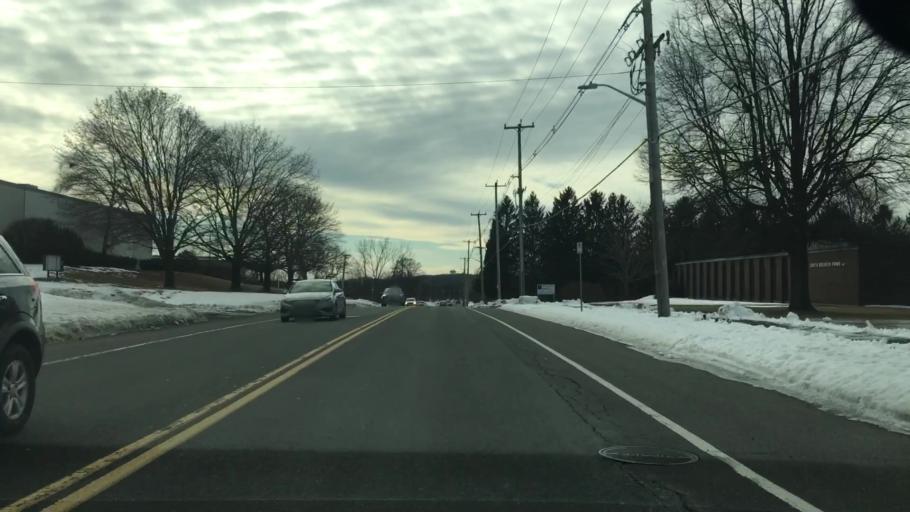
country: US
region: Massachusetts
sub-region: Hampden County
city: Holyoke
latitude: 42.1854
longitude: -72.6358
